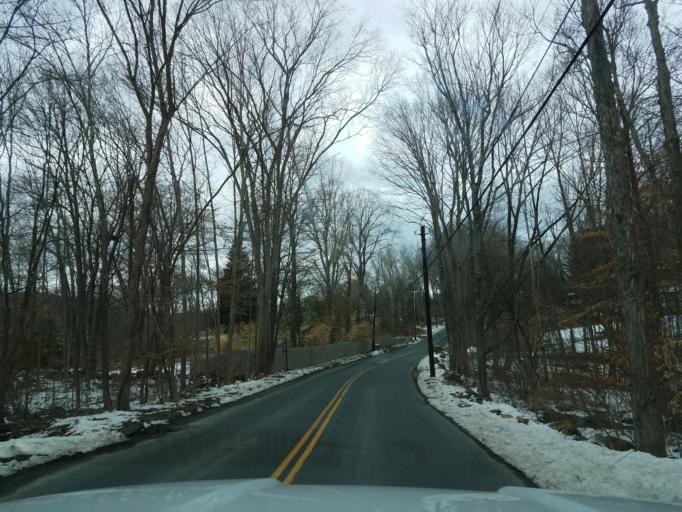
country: US
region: Connecticut
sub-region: Litchfield County
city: New Milford
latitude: 41.6113
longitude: -73.4306
